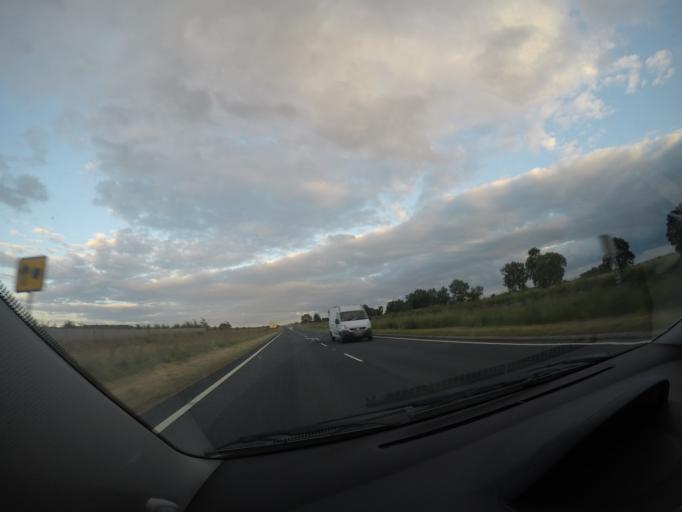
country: GB
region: England
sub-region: North Yorkshire
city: Bedale
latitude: 54.2869
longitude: -1.5456
